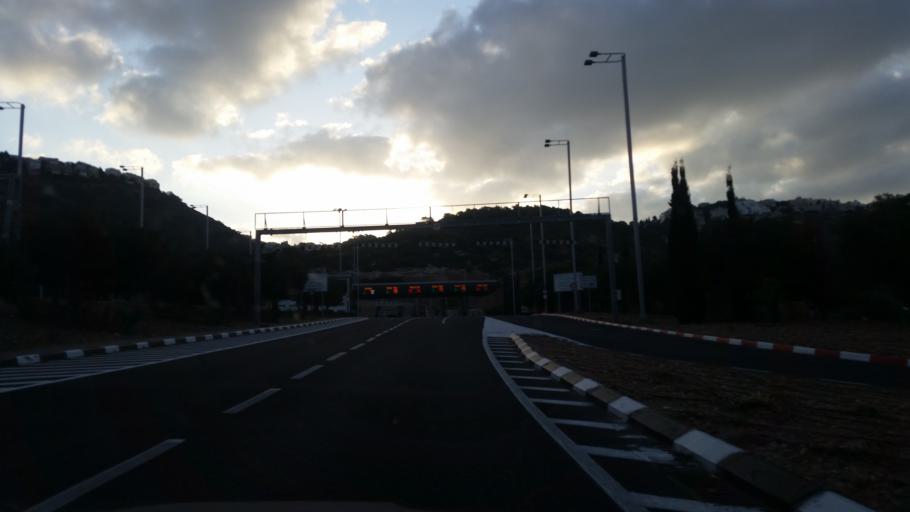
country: IL
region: Haifa
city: Tirat Karmel
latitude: 32.7924
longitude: 34.9676
